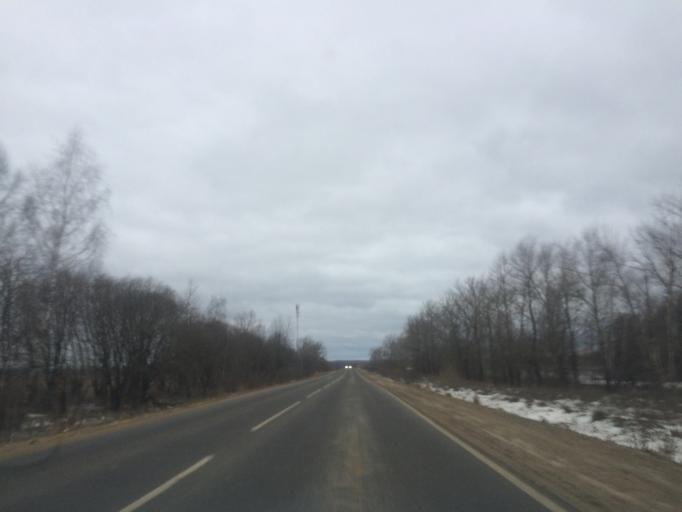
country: RU
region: Tula
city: Odoyev
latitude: 53.9949
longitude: 36.7479
